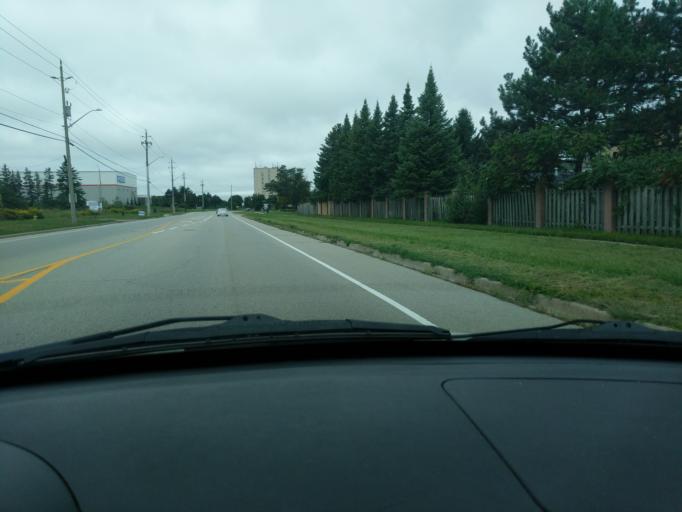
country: CA
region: Ontario
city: Cambridge
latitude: 43.4178
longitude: -80.3015
